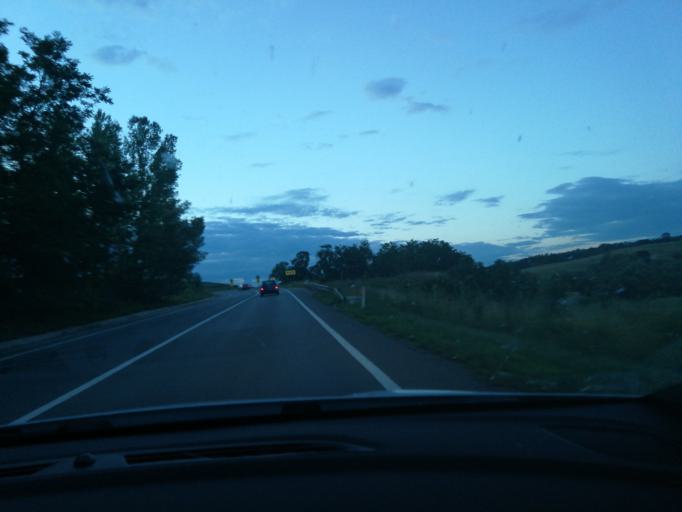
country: RO
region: Brasov
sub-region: Oras Rupea
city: Fiser
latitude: 46.0582
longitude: 25.1787
